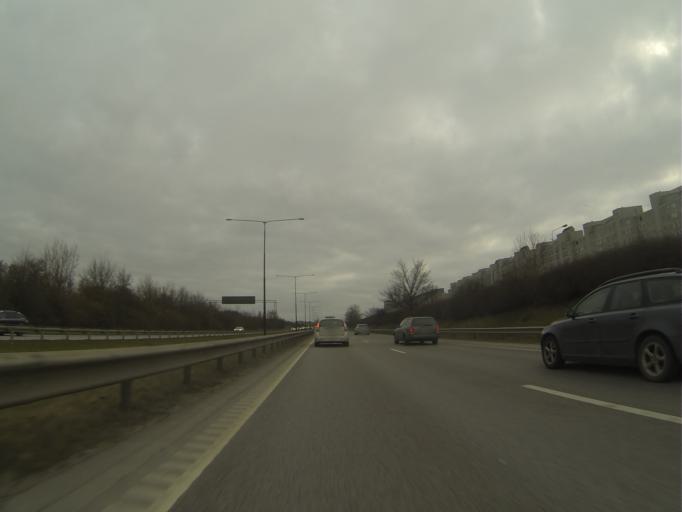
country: SE
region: Skane
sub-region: Burlovs Kommun
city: Arloev
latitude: 55.5912
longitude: 13.0546
